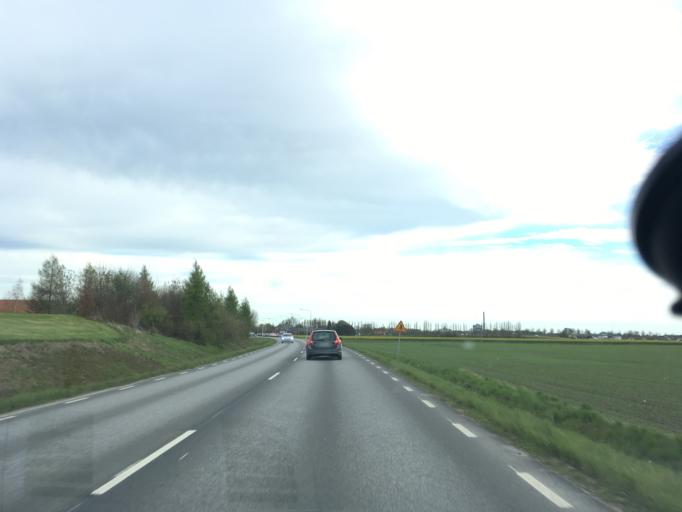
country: SE
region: Skane
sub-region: Lomma Kommun
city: Lomma
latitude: 55.6803
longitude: 13.0957
